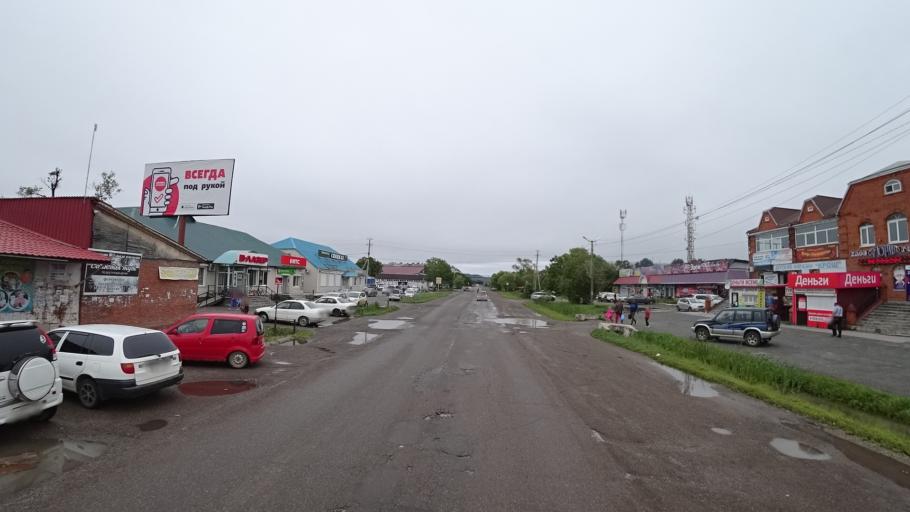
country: RU
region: Primorskiy
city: Monastyrishche
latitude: 44.2056
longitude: 132.4423
